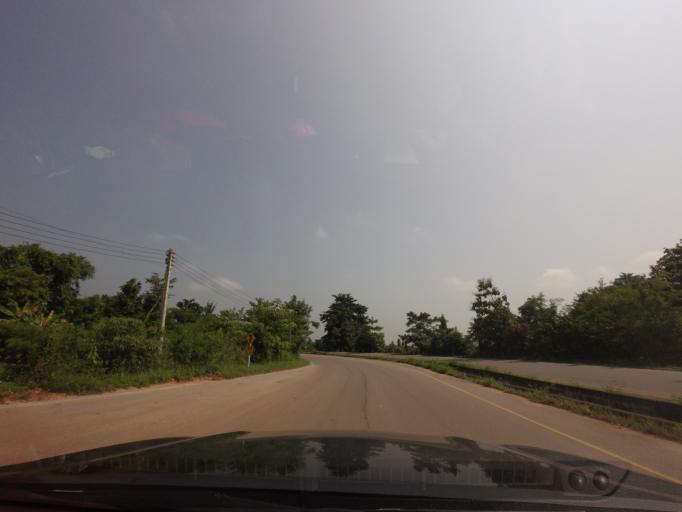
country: TH
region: Nan
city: Nan
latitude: 18.7919
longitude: 100.7543
